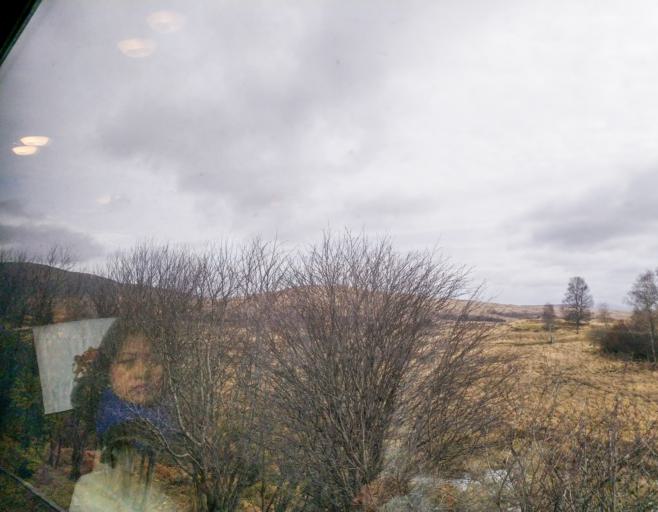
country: GB
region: Scotland
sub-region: Highland
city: Spean Bridge
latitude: 56.6871
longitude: -4.5764
